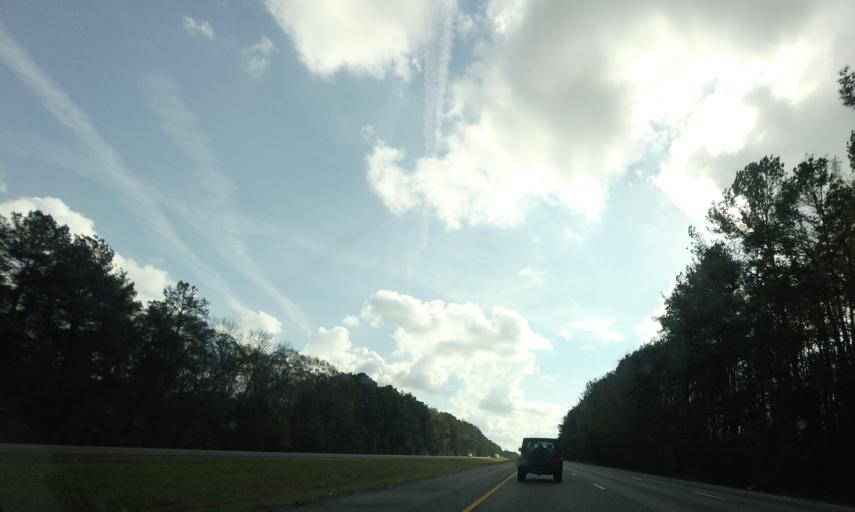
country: US
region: Georgia
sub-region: Houston County
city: Perry
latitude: 32.3630
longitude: -83.7686
